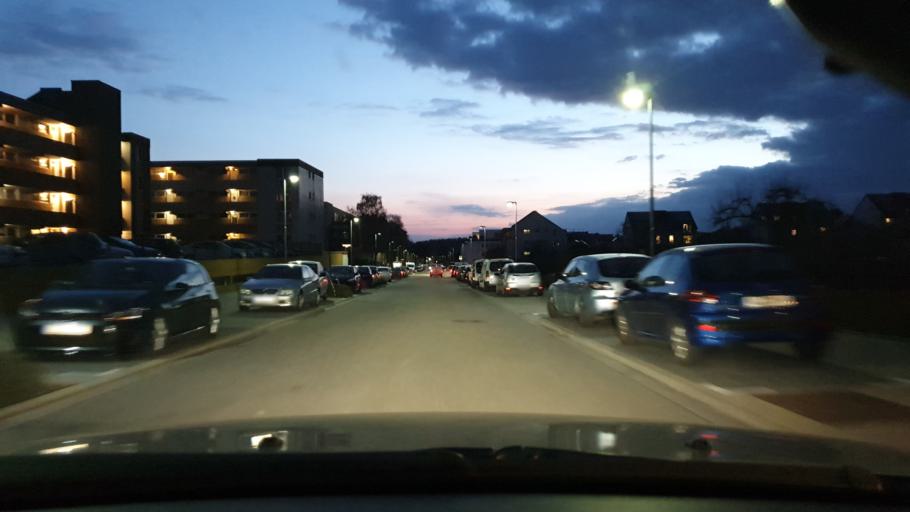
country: DE
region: Rheinland-Pfalz
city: Kaiserslautern
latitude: 49.4541
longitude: 7.7709
